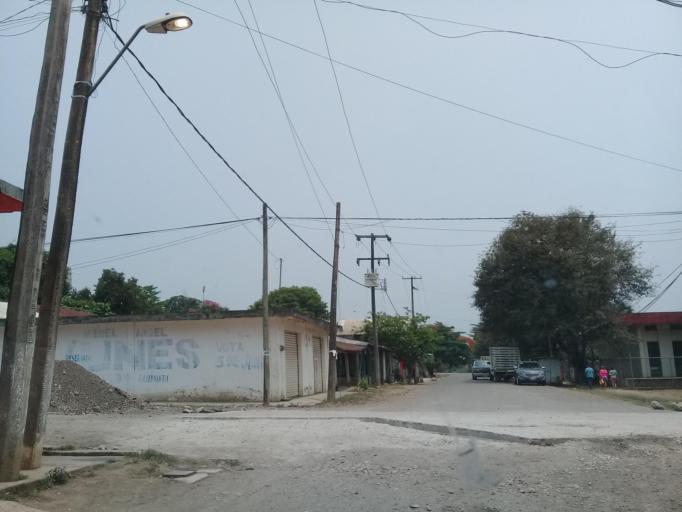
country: MX
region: Veracruz
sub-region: Tezonapa
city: Laguna Chica (Pueblo Nuevo)
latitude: 18.5453
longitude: -96.7350
